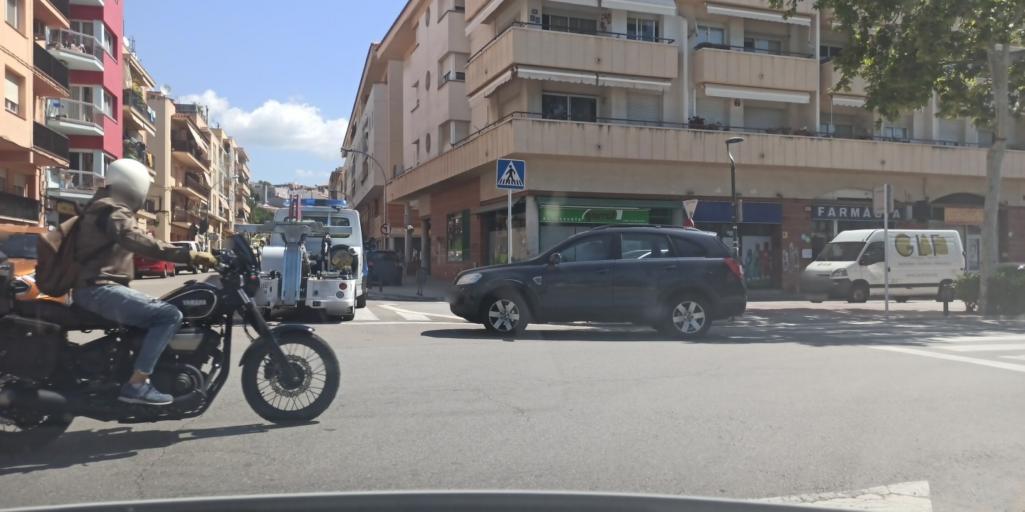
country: ES
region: Catalonia
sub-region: Provincia de Barcelona
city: Sant Pere de Ribes
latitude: 41.2596
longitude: 1.7742
